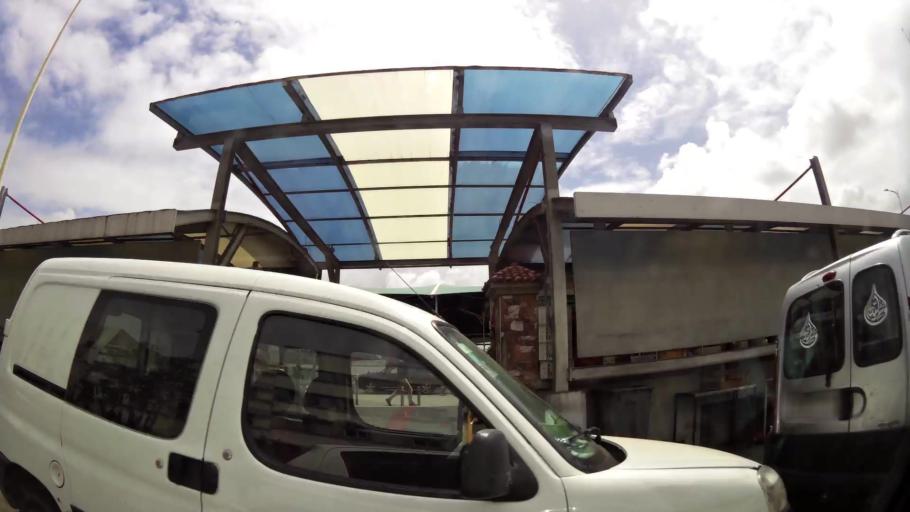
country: MA
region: Grand Casablanca
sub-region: Mediouna
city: Tit Mellil
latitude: 33.6023
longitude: -7.5122
